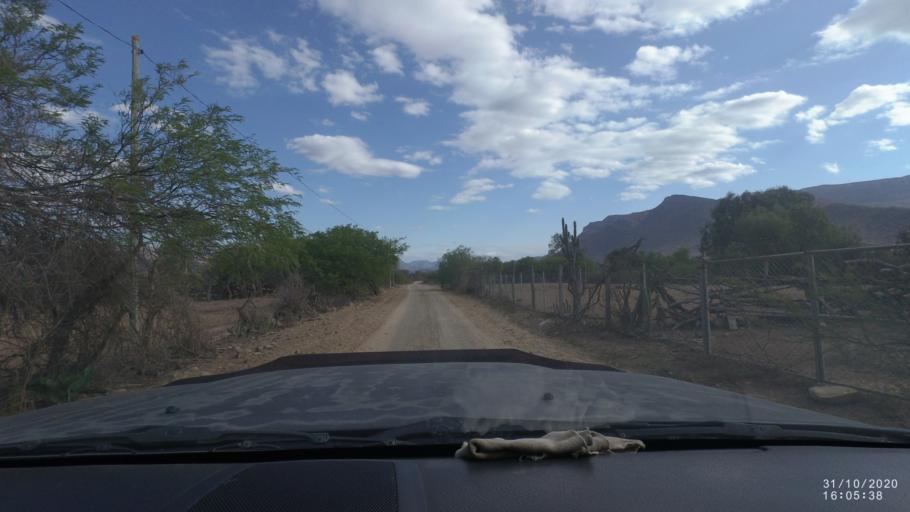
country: BO
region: Chuquisaca
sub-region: Provincia Zudanez
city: Mojocoya
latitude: -18.3680
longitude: -64.6491
